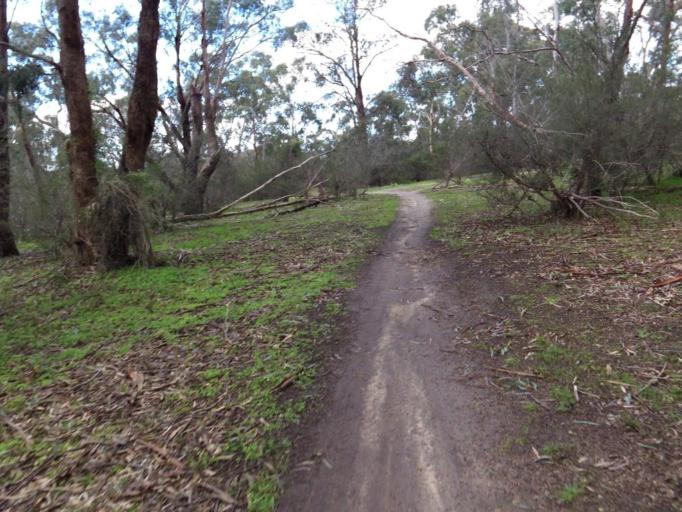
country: AU
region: Victoria
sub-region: Banyule
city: Watsonia North
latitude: -37.6858
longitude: 145.0962
